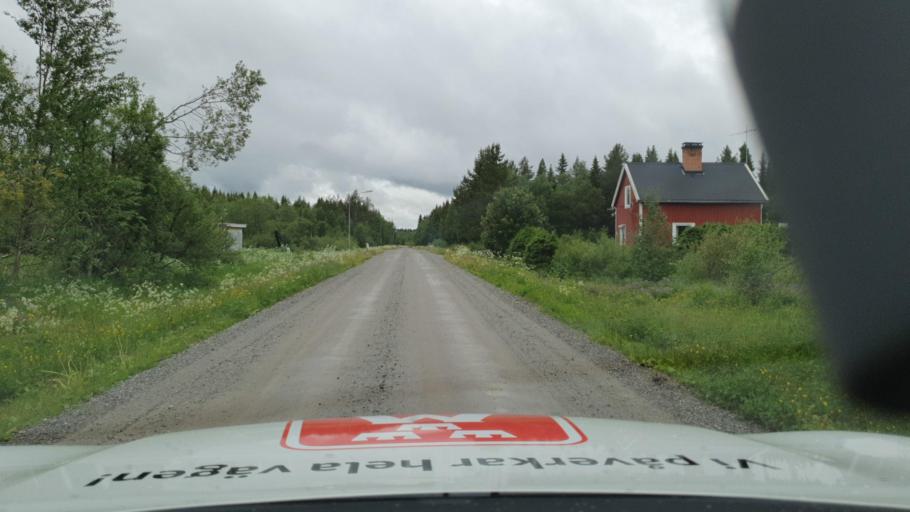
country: SE
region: Vaesterbotten
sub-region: Dorotea Kommun
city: Dorotea
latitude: 64.0892
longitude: 16.6732
